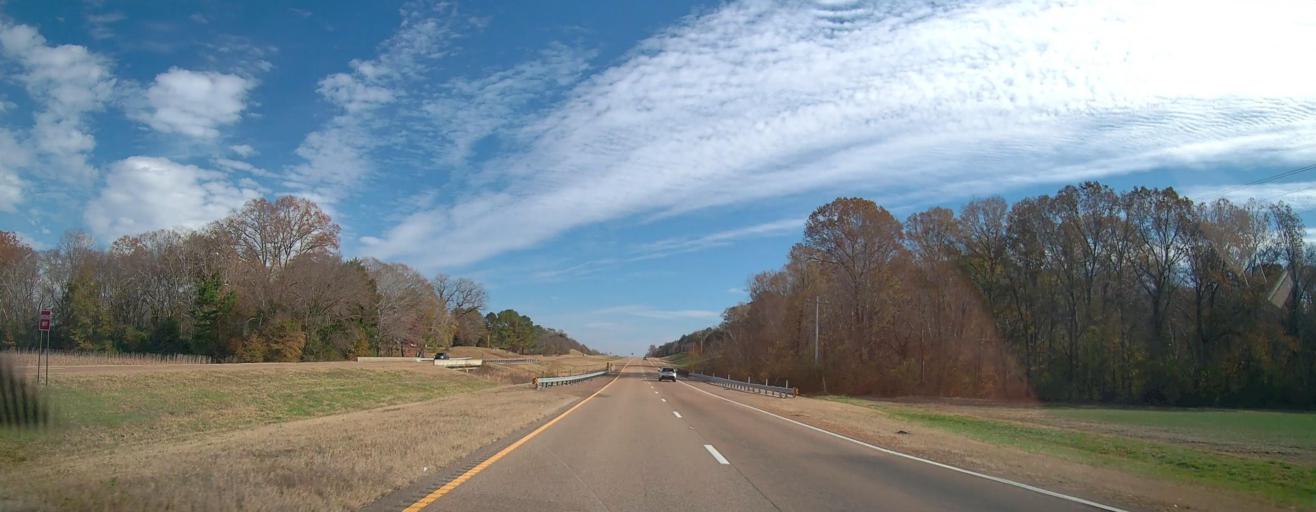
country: US
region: Mississippi
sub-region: Benton County
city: Ashland
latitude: 34.9462
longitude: -89.2461
